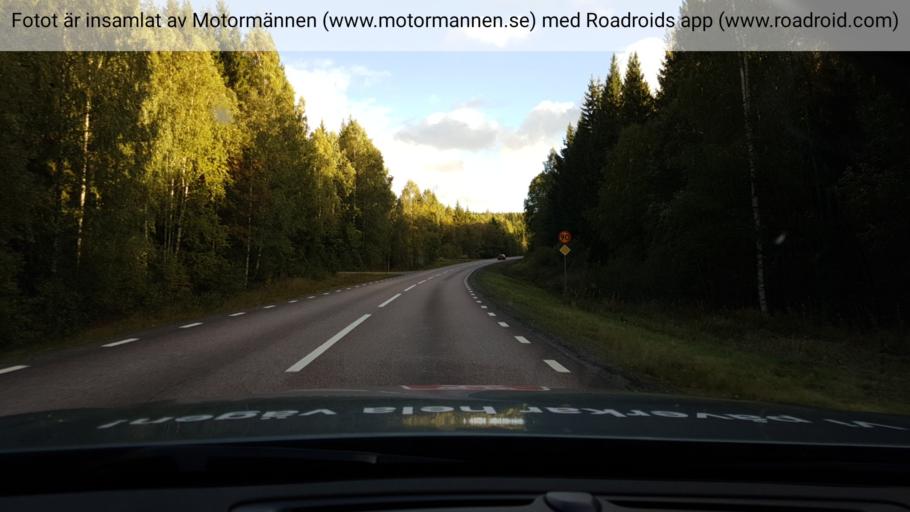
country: SE
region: Vaermland
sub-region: Karlstads Kommun
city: Molkom
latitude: 59.6606
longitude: 13.7077
